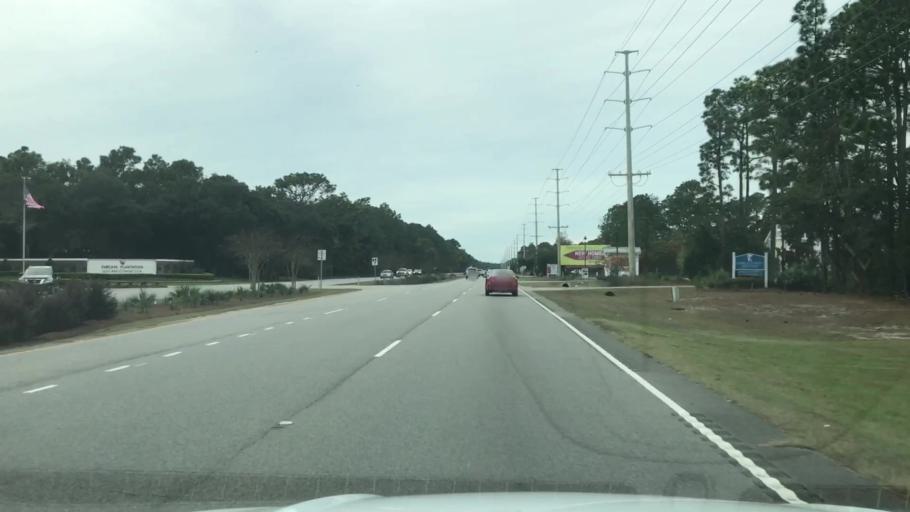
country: US
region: South Carolina
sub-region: Georgetown County
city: Georgetown
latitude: 33.4257
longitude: -79.1579
